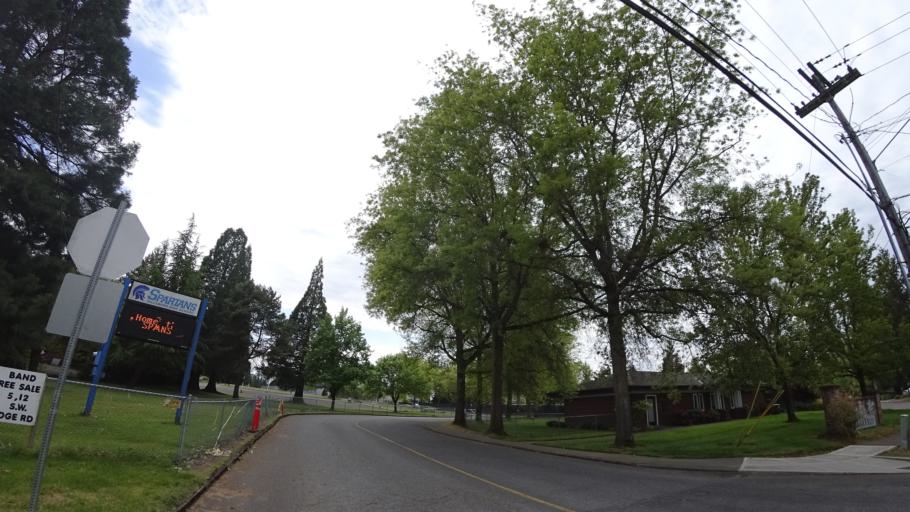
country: US
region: Oregon
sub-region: Washington County
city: Hillsboro
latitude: 45.4962
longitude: -122.9545
